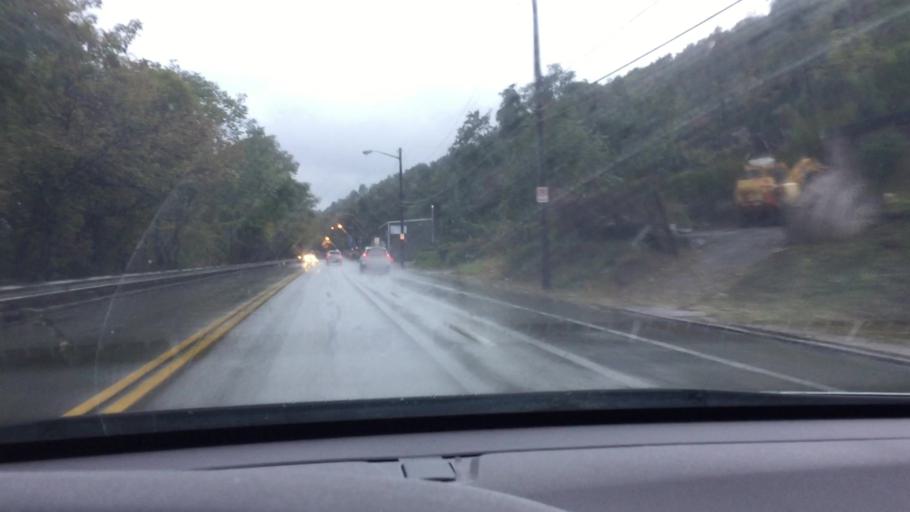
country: US
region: Pennsylvania
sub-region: Allegheny County
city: Homestead
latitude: 40.4172
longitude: -79.9473
